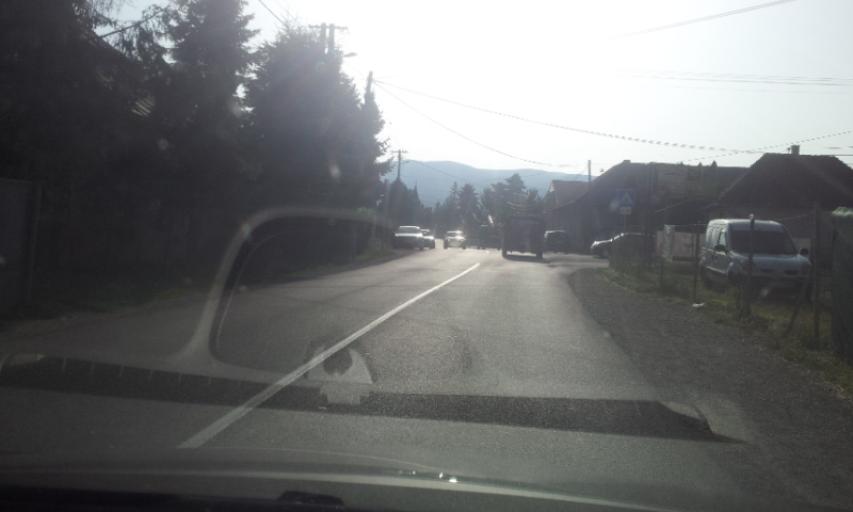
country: SK
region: Kosicky
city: Kosice
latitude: 48.6043
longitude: 21.3460
